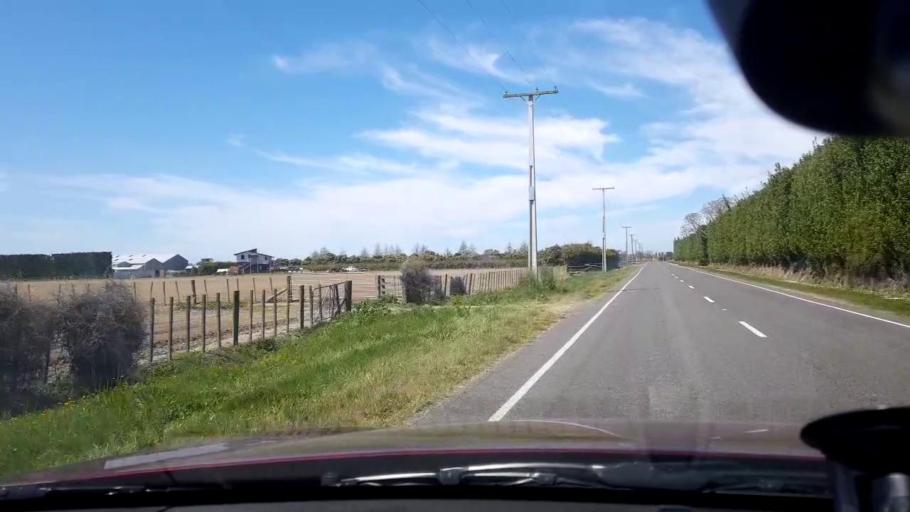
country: NZ
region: Gisborne
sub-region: Gisborne District
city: Gisborne
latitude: -38.6271
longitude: 177.9247
